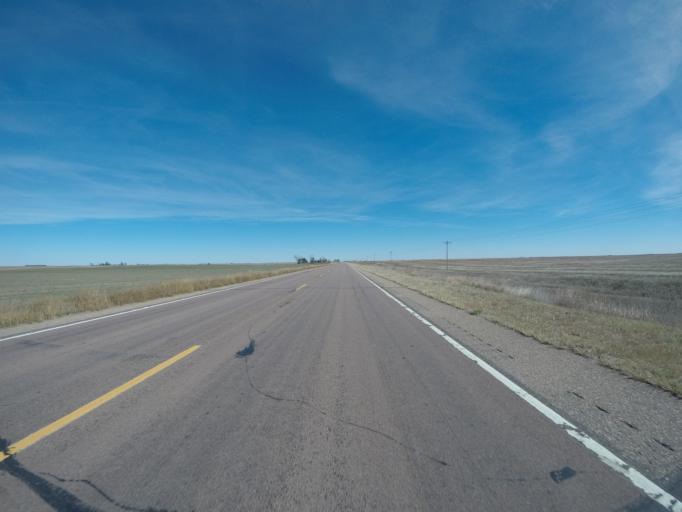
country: US
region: Colorado
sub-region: Yuma County
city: Yuma
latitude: 39.6559
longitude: -102.6654
